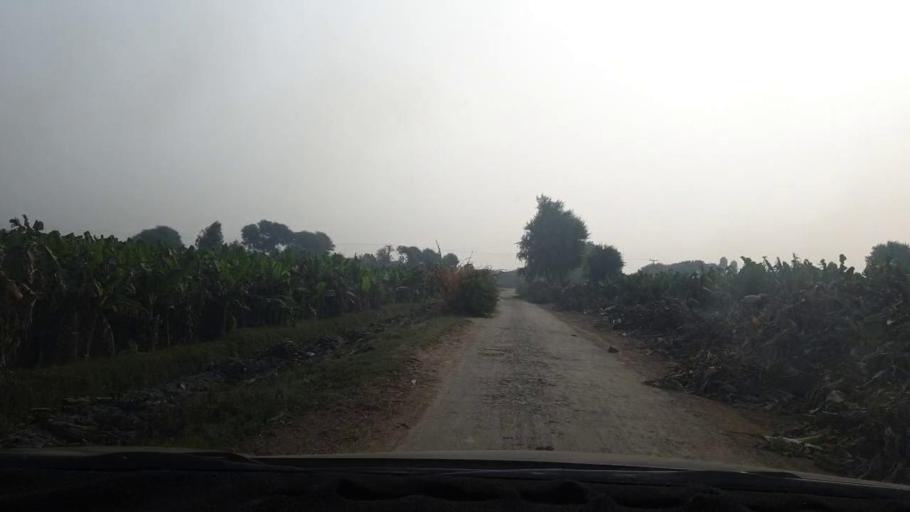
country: PK
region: Sindh
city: Matiari
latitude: 25.5915
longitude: 68.5473
